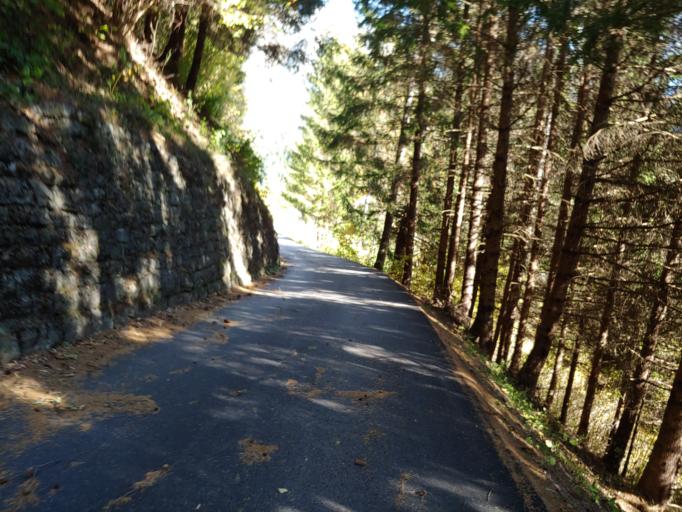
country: IT
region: Veneto
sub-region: Provincia di Belluno
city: Lozzo di Cadore
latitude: 46.4908
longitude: 12.4482
